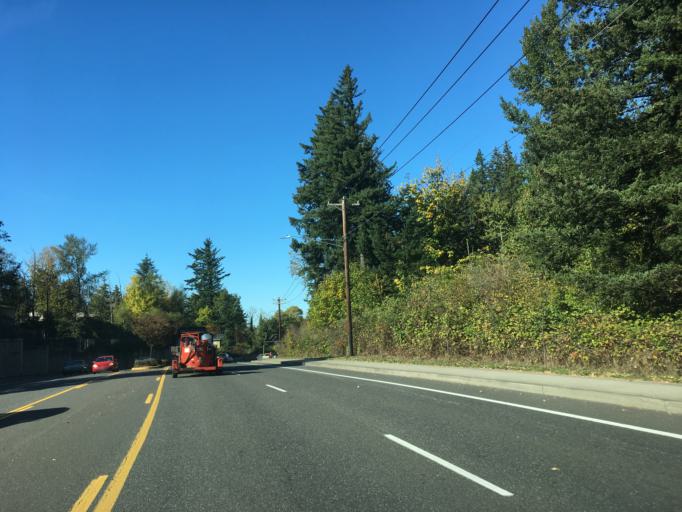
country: US
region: Oregon
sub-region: Multnomah County
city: Gresham
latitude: 45.4998
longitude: -122.3990
